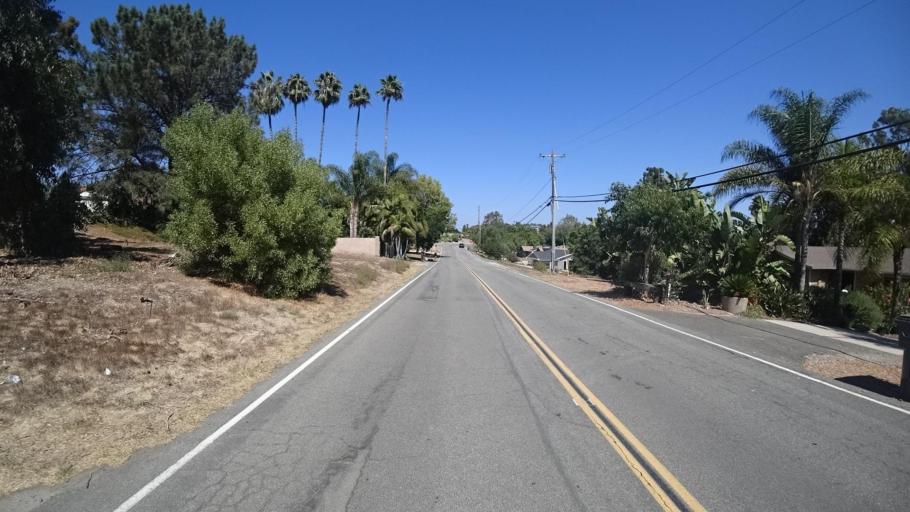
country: US
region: California
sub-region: San Diego County
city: Lake San Marcos
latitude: 33.1375
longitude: -117.2208
